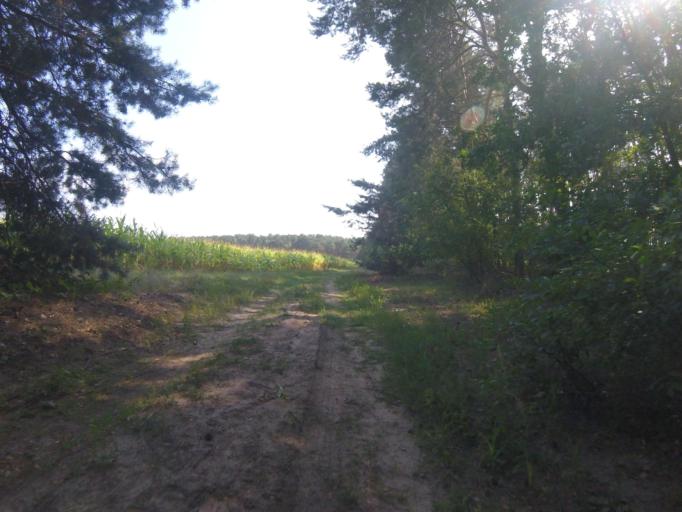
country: DE
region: Brandenburg
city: Bestensee
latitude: 52.2765
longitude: 13.7492
